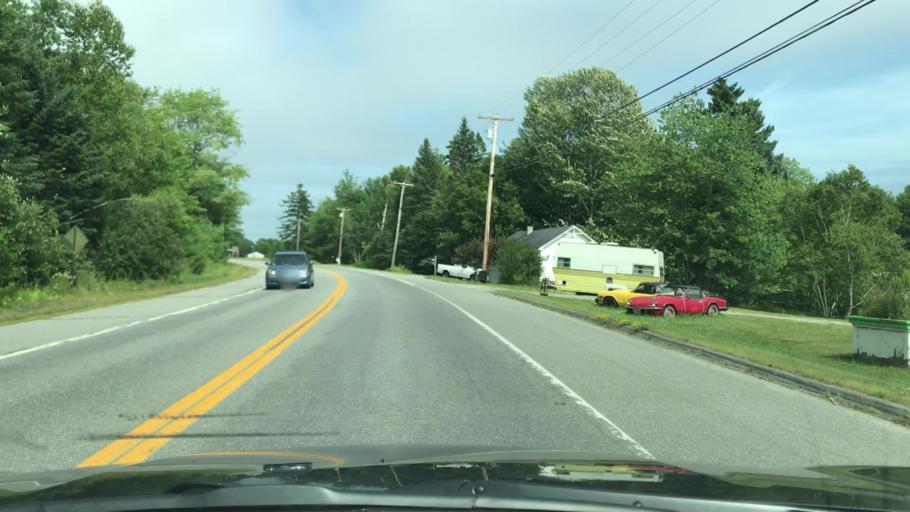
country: US
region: Maine
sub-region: Waldo County
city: Stockton Springs
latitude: 44.4933
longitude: -68.8464
